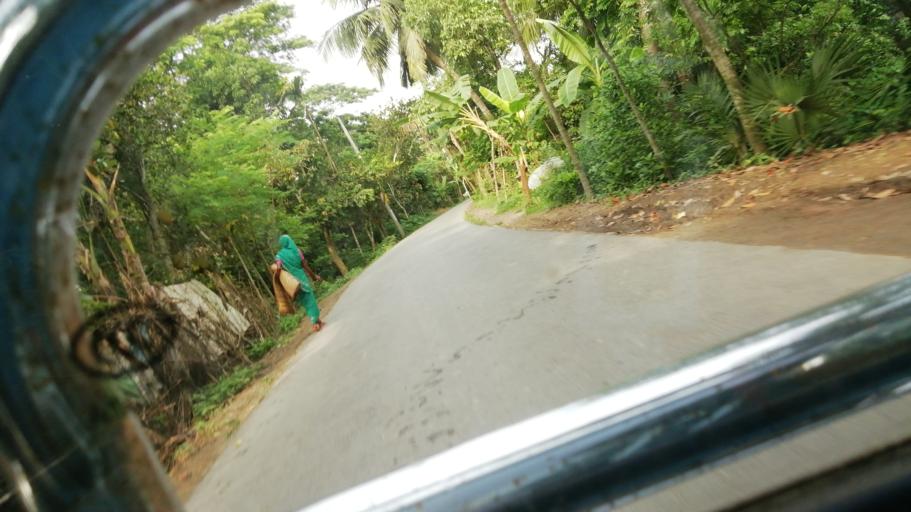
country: BD
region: Khulna
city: Kesabpur
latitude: 23.0277
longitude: 89.2660
